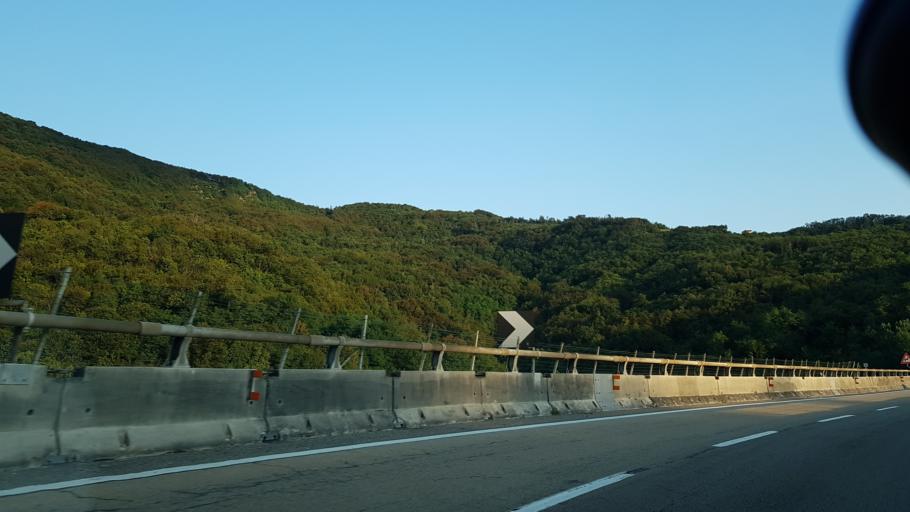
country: IT
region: Liguria
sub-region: Provincia di Genova
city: Busalla
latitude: 44.5409
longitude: 8.9460
